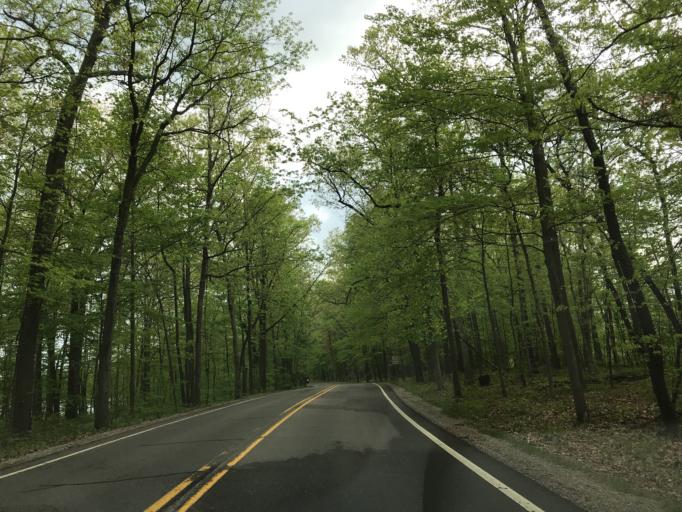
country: US
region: Michigan
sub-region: Oakland County
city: South Lyon
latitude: 42.5332
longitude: -83.6618
